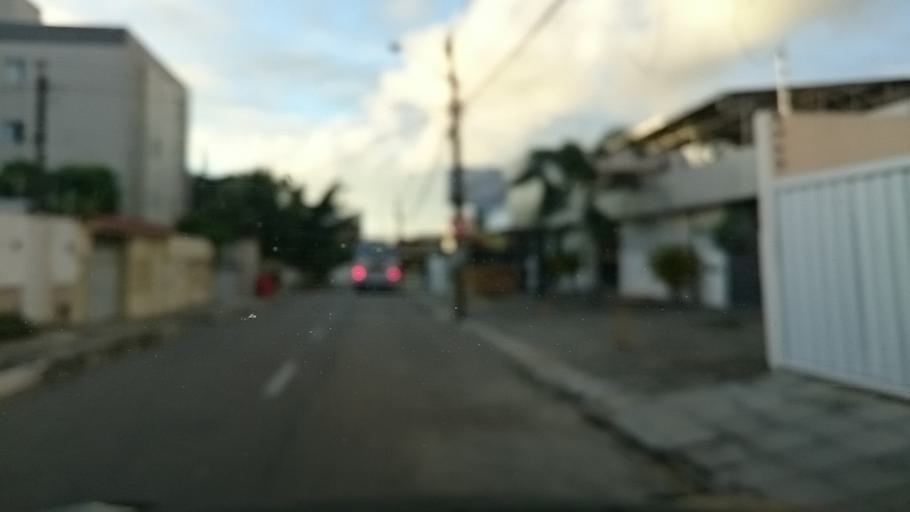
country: BR
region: Paraiba
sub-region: Joao Pessoa
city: Joao Pessoa
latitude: -7.1515
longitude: -34.8376
